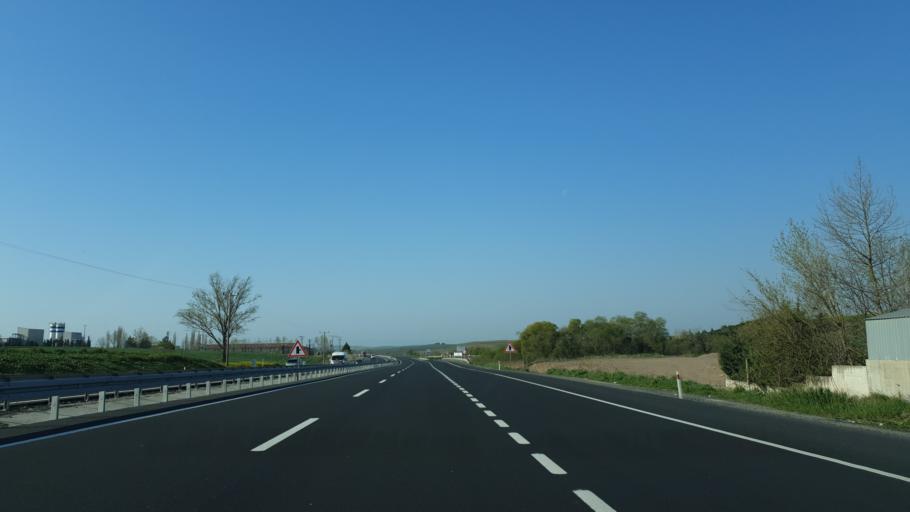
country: TR
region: Tekirdag
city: Corlu
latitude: 41.1238
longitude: 27.7534
